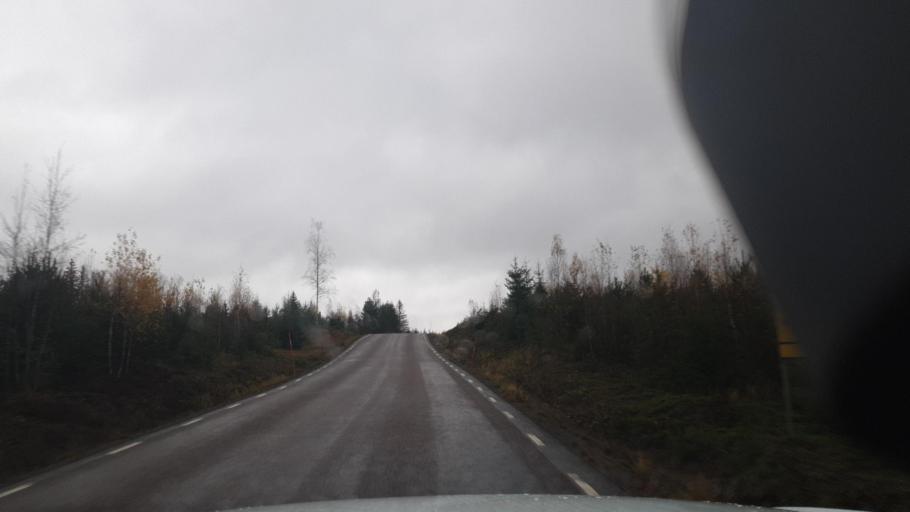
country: SE
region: Vaermland
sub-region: Eda Kommun
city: Charlottenberg
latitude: 59.7926
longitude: 12.2294
